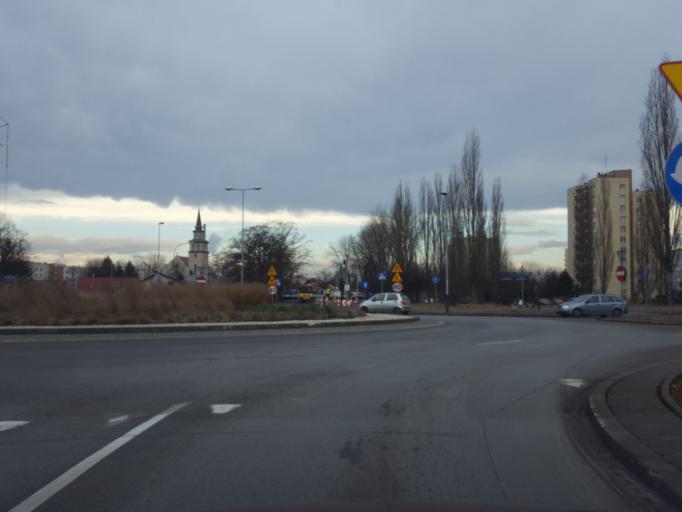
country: PL
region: Lesser Poland Voivodeship
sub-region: Krakow
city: Krakow
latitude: 50.0760
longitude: 20.0134
